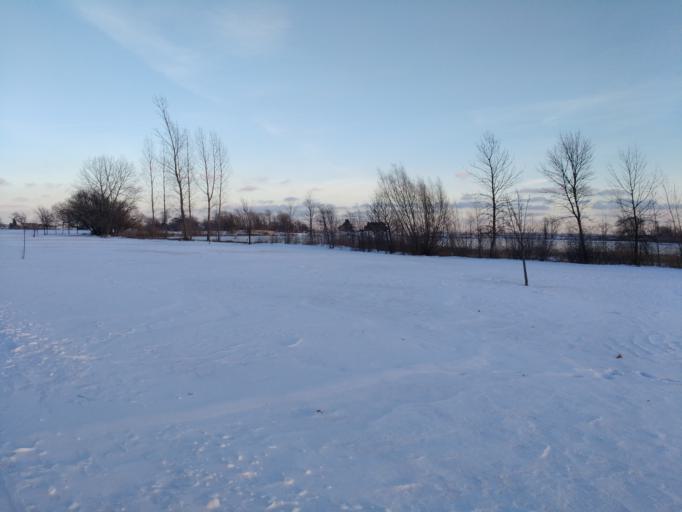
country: US
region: Michigan
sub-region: Delta County
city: Escanaba
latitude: 45.7393
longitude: -87.0533
